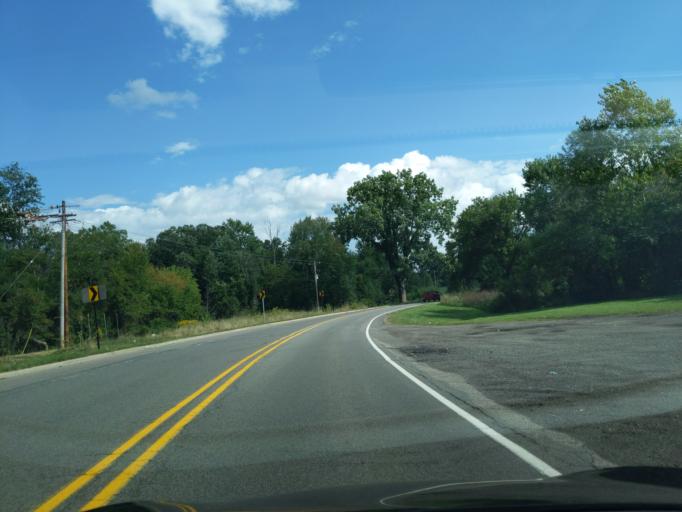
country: US
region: Michigan
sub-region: Jackson County
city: Jackson
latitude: 42.2863
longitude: -84.4615
